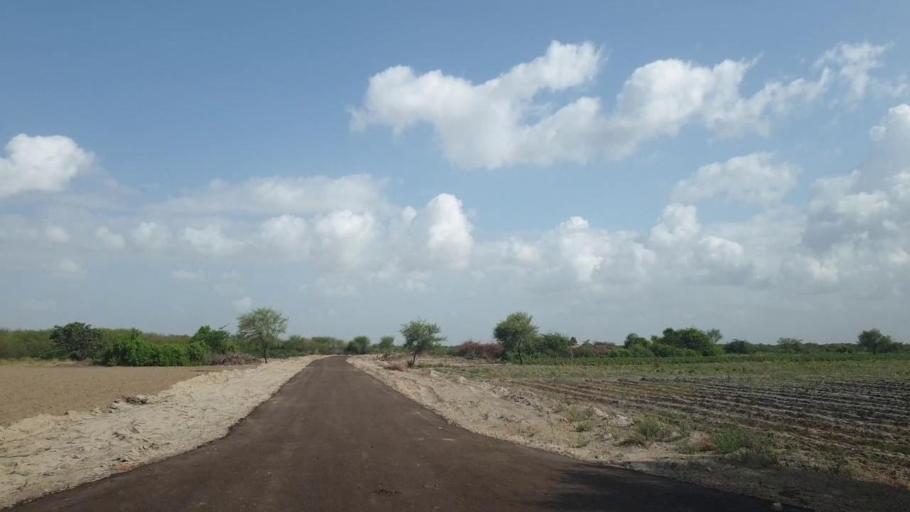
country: PK
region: Sindh
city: Kadhan
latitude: 24.5393
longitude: 69.0660
